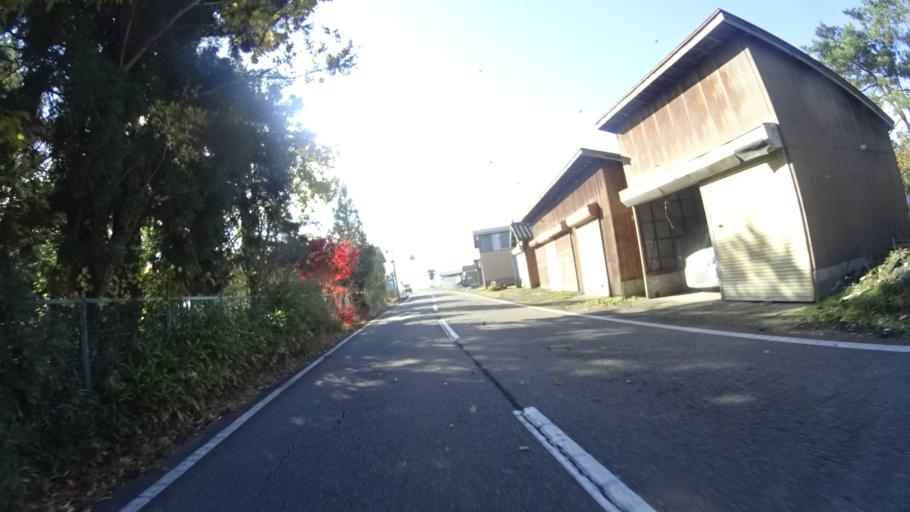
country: JP
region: Niigata
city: Mitsuke
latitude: 37.5578
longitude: 138.8493
